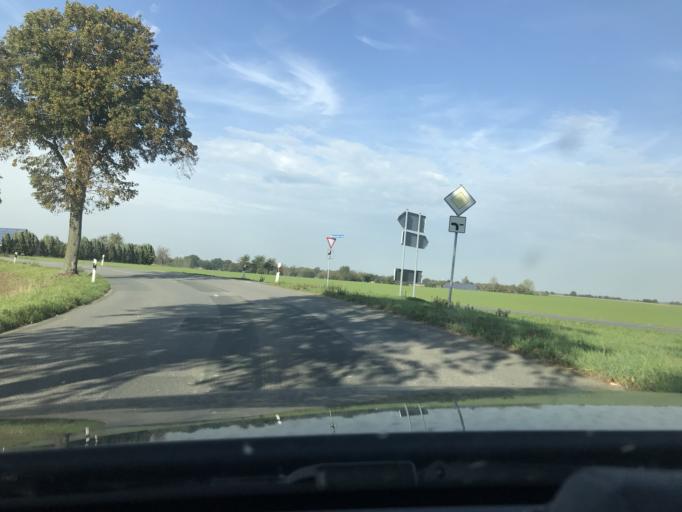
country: DE
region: North Rhine-Westphalia
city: Kalkar
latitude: 51.7166
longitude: 6.2712
